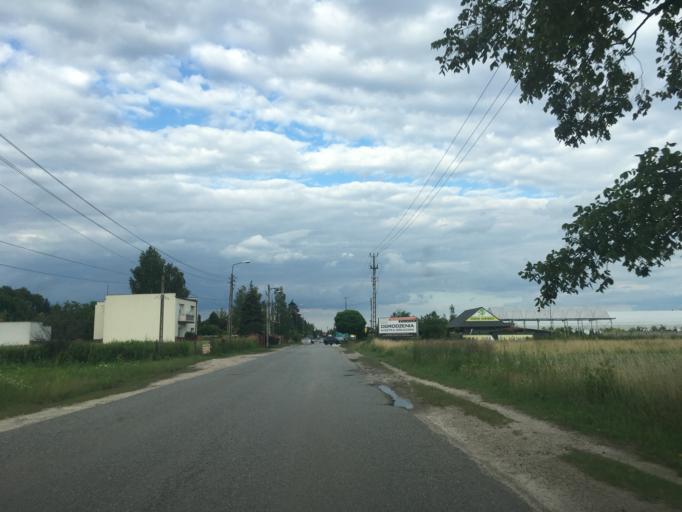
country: PL
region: Masovian Voivodeship
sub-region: Powiat piaseczynski
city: Mysiadlo
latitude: 52.1100
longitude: 21.0012
